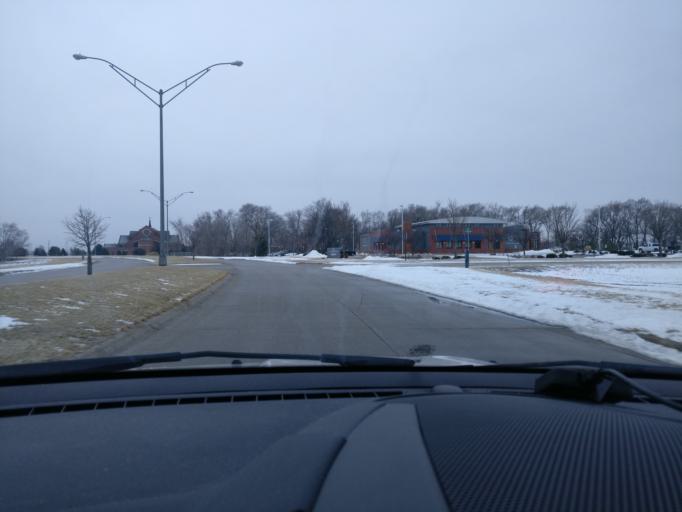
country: US
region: Nebraska
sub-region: Dodge County
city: Fremont
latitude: 41.4491
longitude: -96.4544
